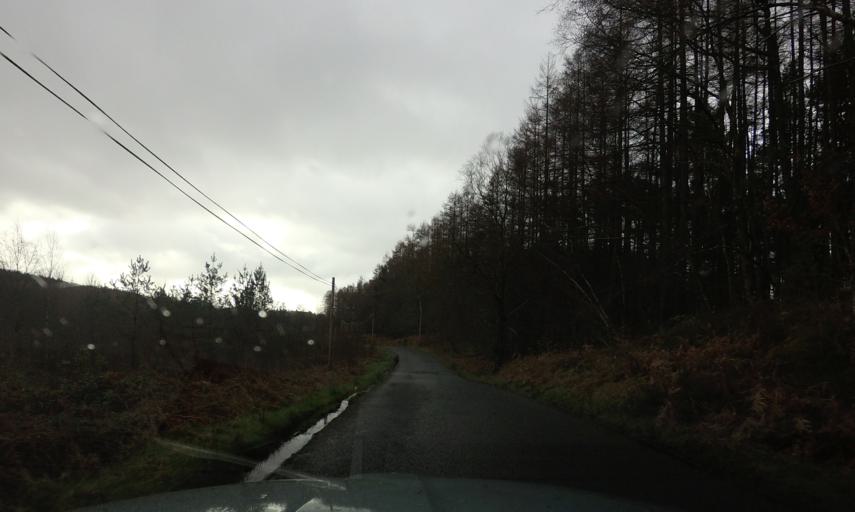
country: GB
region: Scotland
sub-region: West Dunbartonshire
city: Balloch
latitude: 56.1451
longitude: -4.6382
